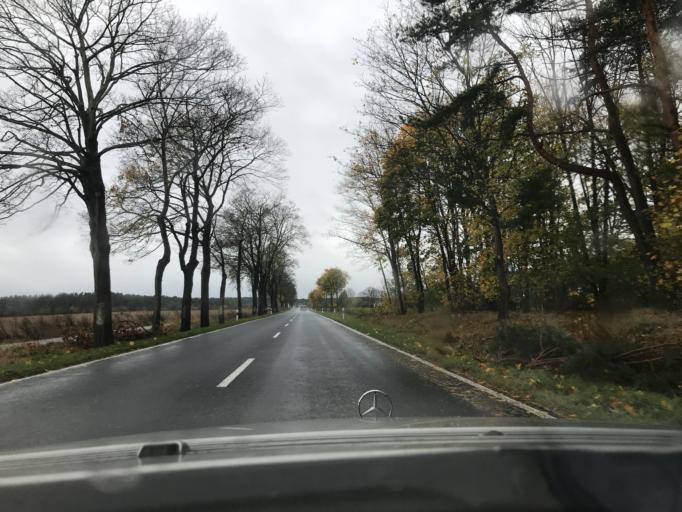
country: DE
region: Brandenburg
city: Trebbin
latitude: 52.2153
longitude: 13.1607
